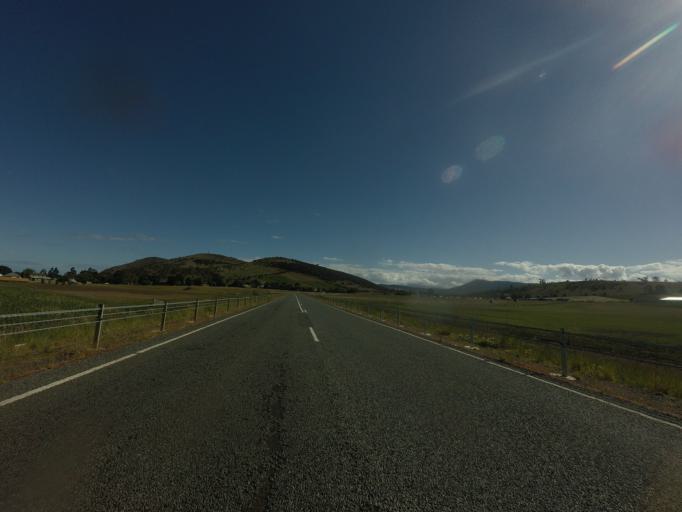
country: AU
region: Tasmania
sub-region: Clarence
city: Cambridge
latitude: -42.7339
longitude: 147.4311
